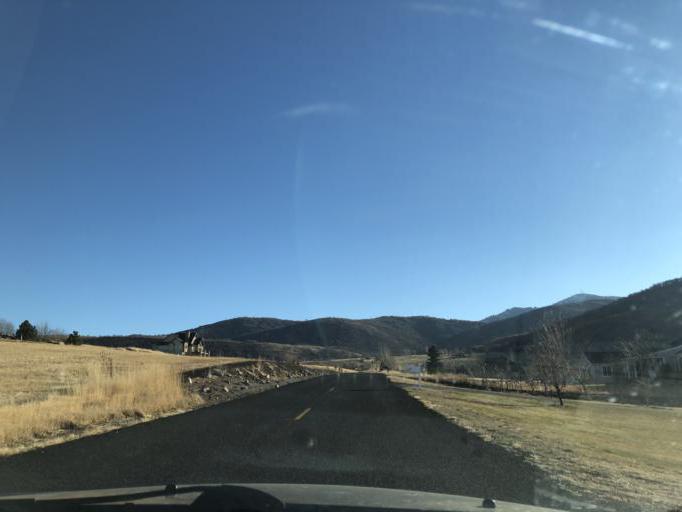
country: US
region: Utah
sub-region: Cache County
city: Wellsville
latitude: 41.5859
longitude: -111.9259
